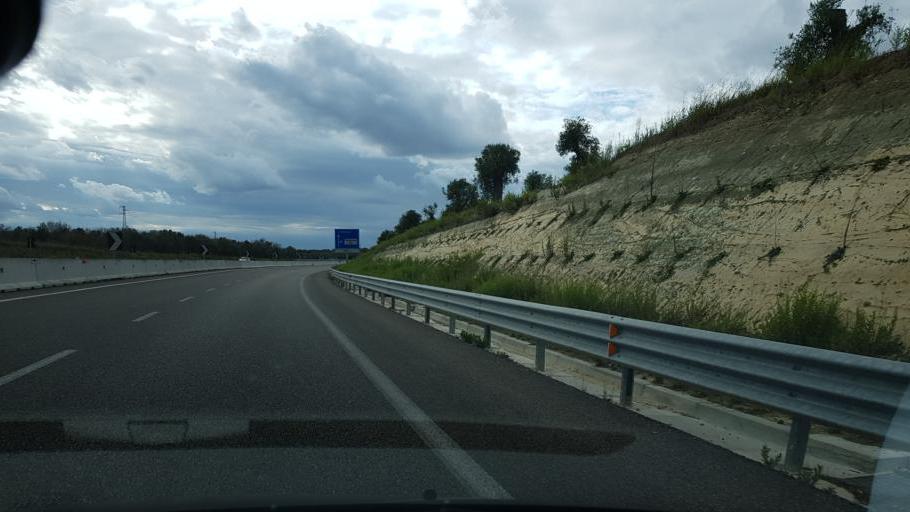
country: IT
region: Apulia
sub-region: Provincia di Lecce
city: Palmariggi
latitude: 40.1264
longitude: 18.3809
